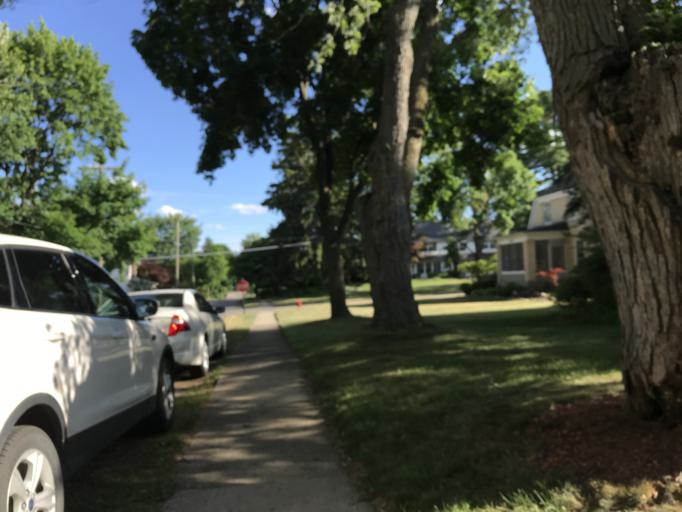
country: US
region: Michigan
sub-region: Oakland County
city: Farmington
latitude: 42.4662
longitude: -83.3828
